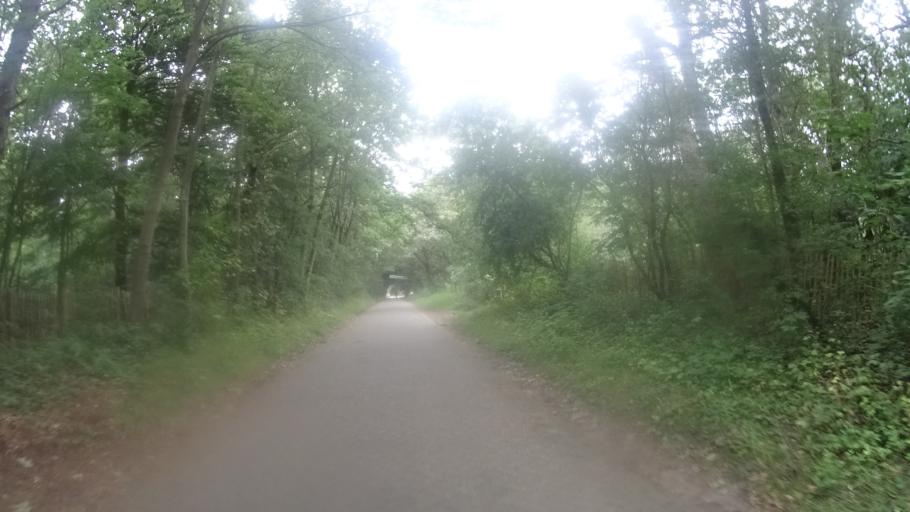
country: NL
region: North Holland
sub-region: Gemeente Castricum
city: Castricum
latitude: 52.5593
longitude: 4.6362
